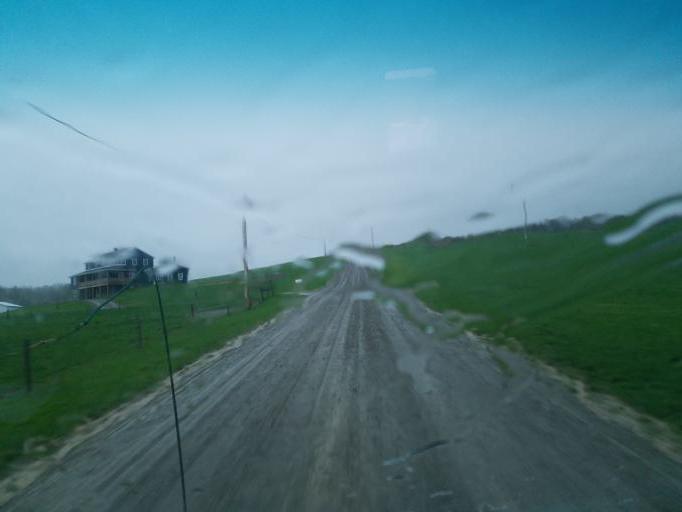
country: US
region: Pennsylvania
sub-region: Potter County
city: Galeton
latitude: 41.9015
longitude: -77.7414
